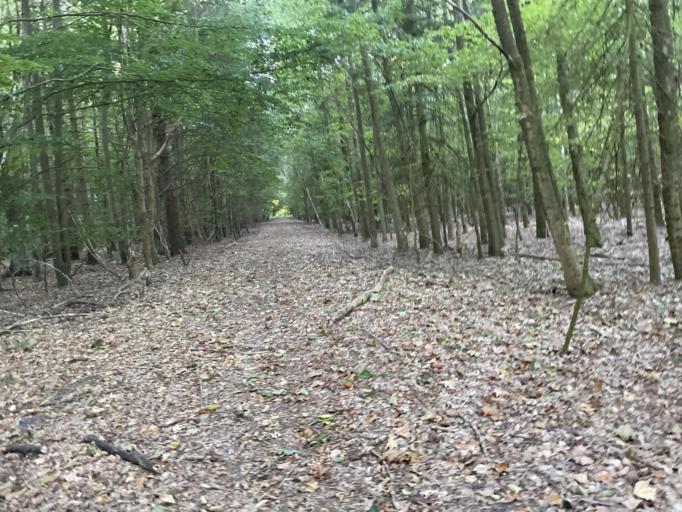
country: DE
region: Schleswig-Holstein
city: Mildstedt
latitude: 54.4737
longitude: 9.1120
